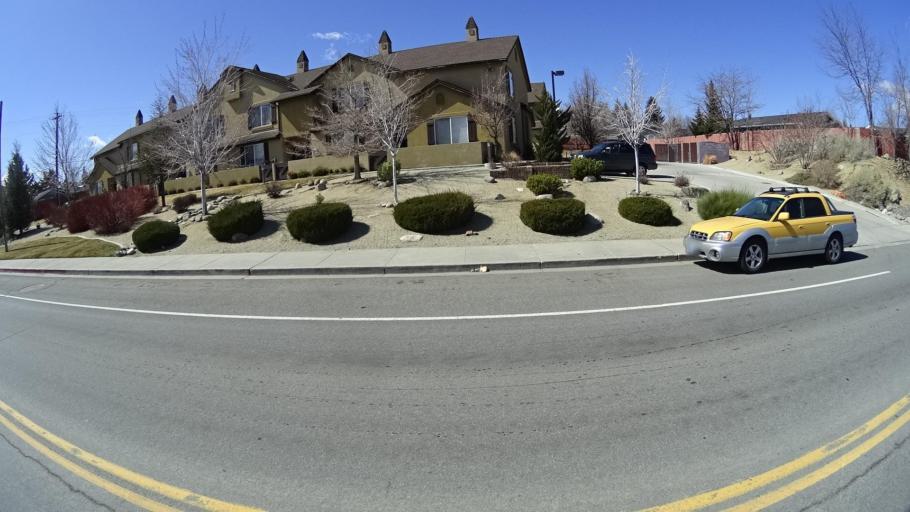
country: US
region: Nevada
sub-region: Washoe County
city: Golden Valley
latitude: 39.5931
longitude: -119.8360
